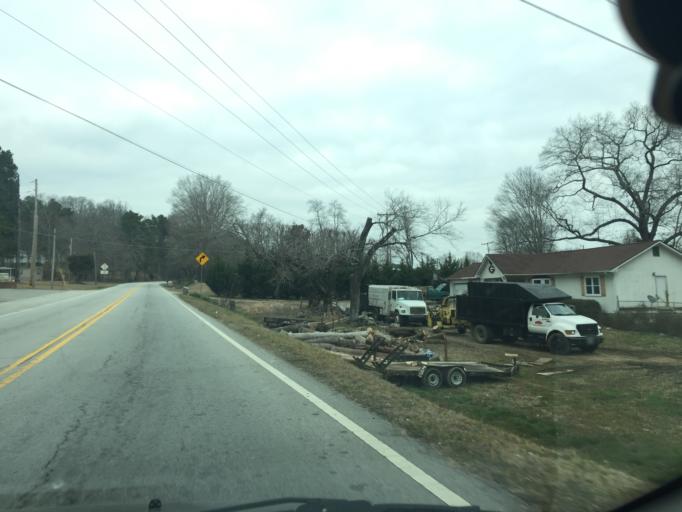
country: US
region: Georgia
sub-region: Catoosa County
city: Indian Springs
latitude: 34.9690
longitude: -85.1826
